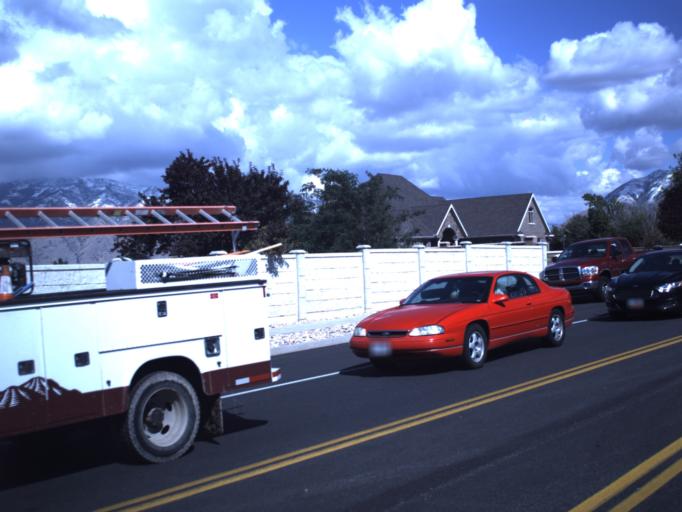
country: US
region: Utah
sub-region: Utah County
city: Spanish Fork
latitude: 40.1153
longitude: -111.6308
